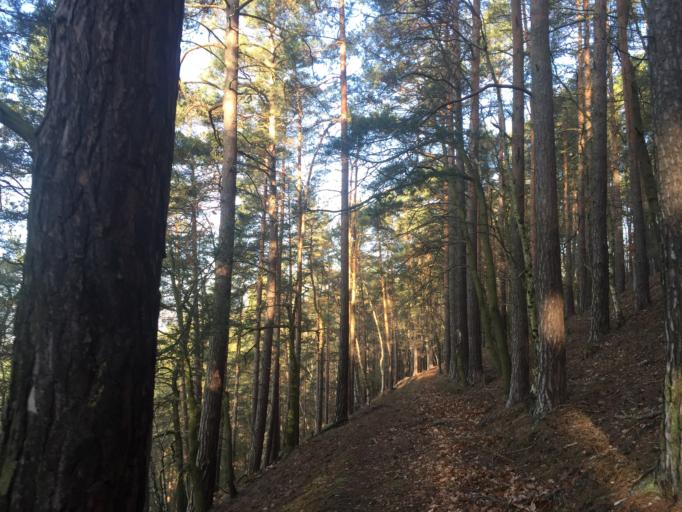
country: DE
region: Thuringia
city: Freienorla
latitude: 50.7574
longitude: 11.5359
